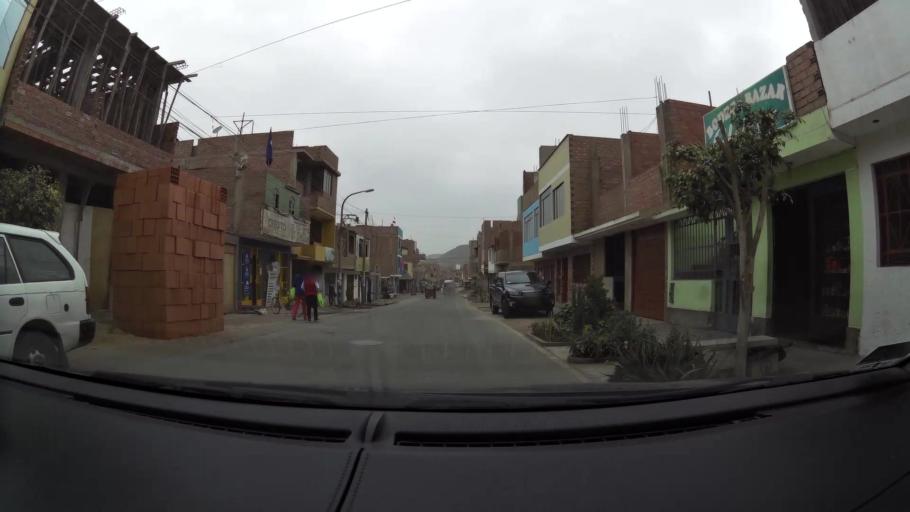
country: PE
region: Lima
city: Ventanilla
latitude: -11.9229
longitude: -77.0824
